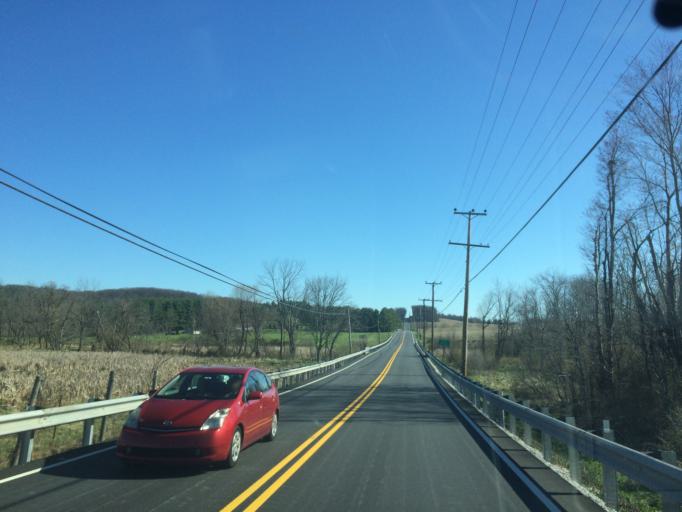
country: US
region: Maryland
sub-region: Carroll County
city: Westminster
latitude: 39.6330
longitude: -76.9897
